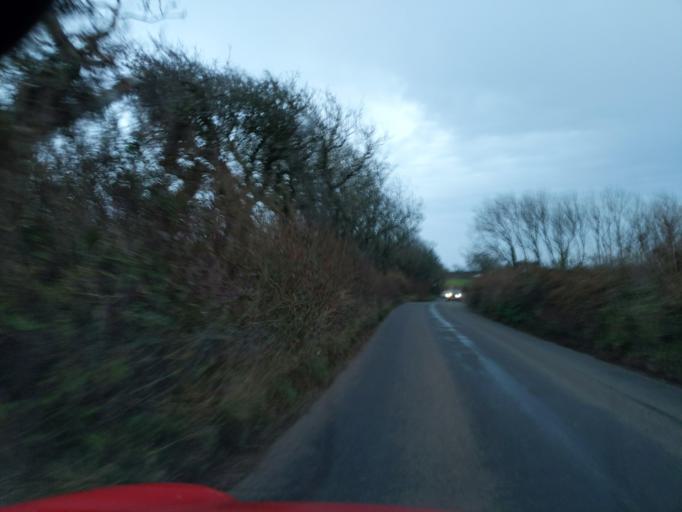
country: GB
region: England
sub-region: Devon
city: Wembury
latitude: 50.3333
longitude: -4.0663
